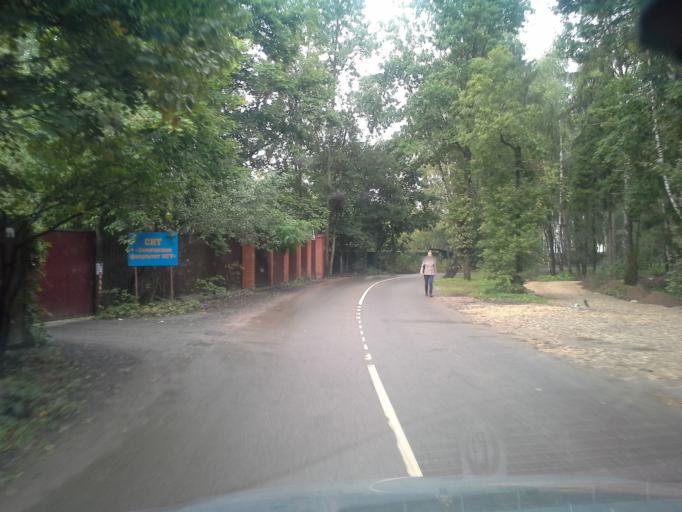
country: RU
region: Moskovskaya
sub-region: Leninskiy Rayon
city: Vnukovo
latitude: 55.6320
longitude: 37.3076
